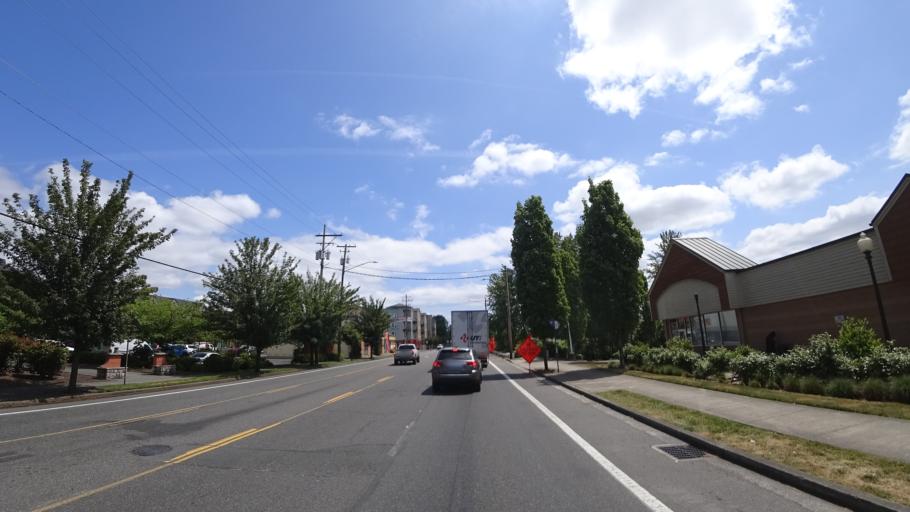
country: US
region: Washington
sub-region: Clark County
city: Vancouver
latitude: 45.6031
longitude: -122.6773
